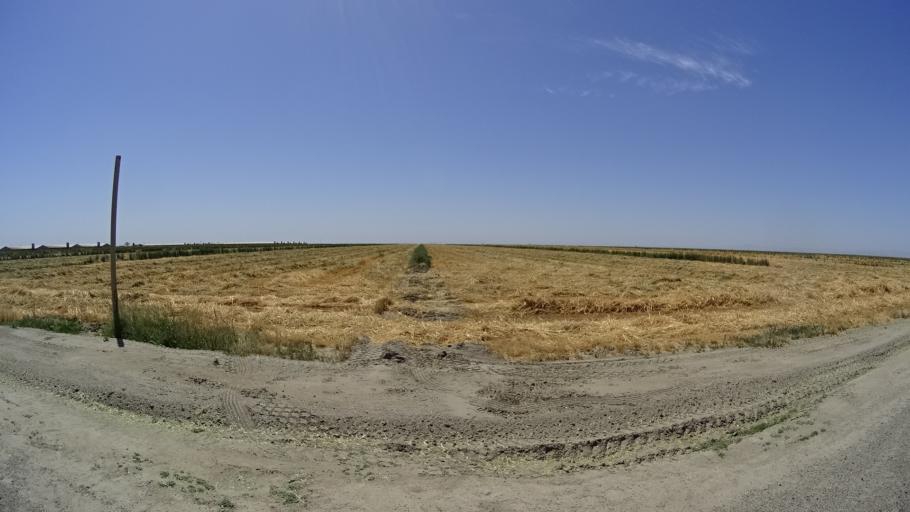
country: US
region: California
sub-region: Kings County
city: Corcoran
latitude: 36.1379
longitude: -119.6705
